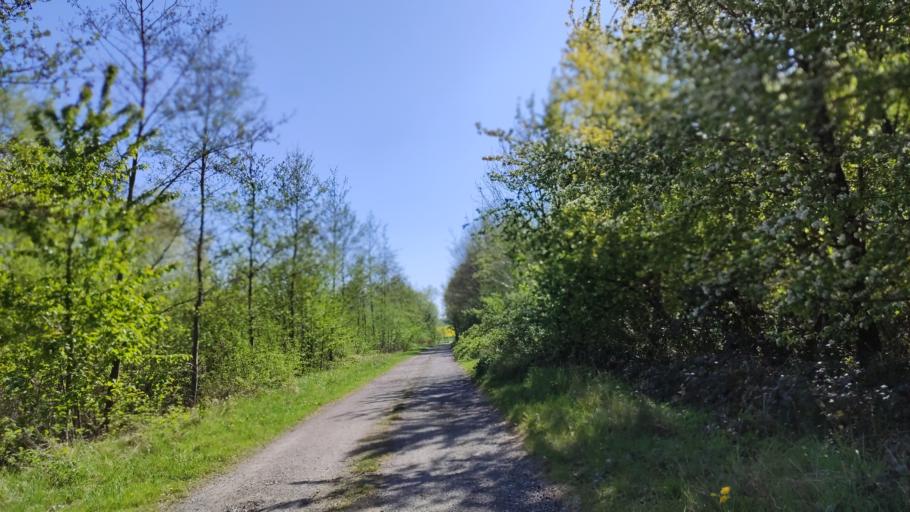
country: DE
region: Lower Saxony
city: Boffzen
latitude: 51.7471
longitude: 9.3630
